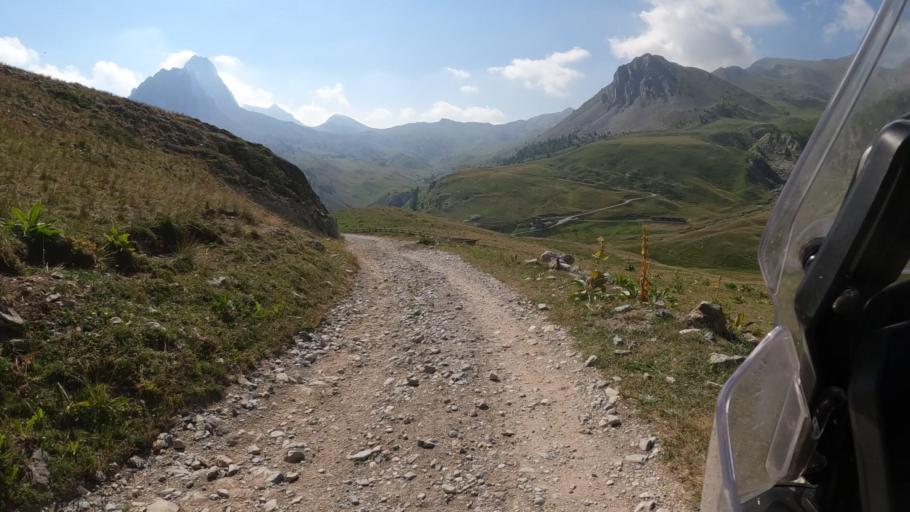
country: IT
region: Piedmont
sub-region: Provincia di Cuneo
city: Pietraporzio
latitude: 44.4026
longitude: 7.0362
